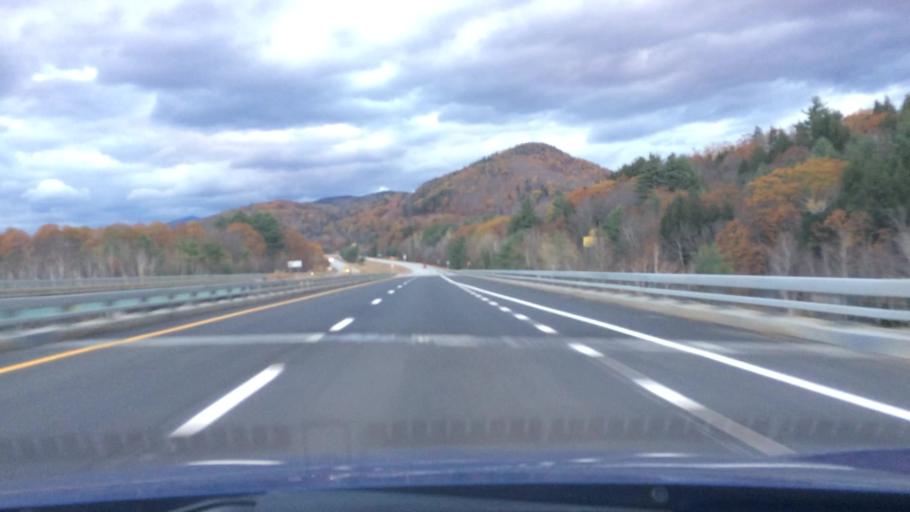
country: US
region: New Hampshire
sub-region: Grafton County
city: Woodstock
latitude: 43.9595
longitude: -71.6795
